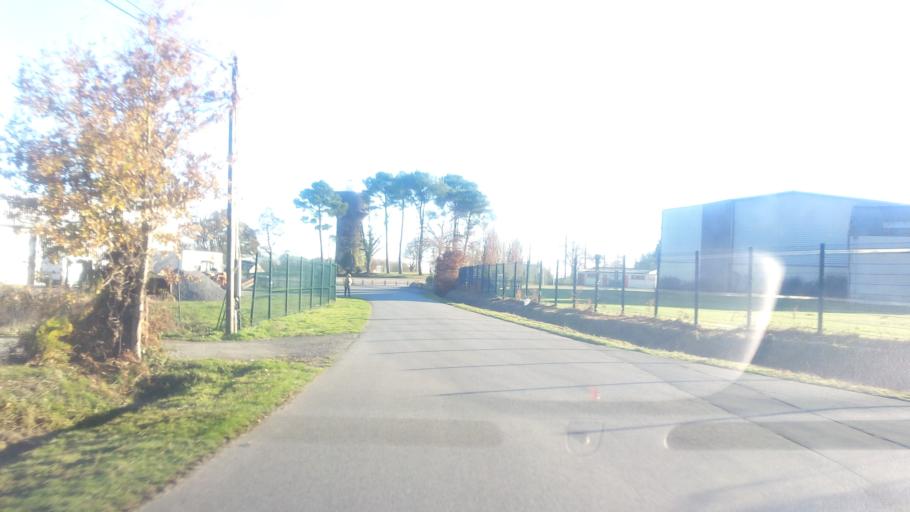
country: FR
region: Brittany
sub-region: Departement du Morbihan
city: Peillac
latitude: 47.7185
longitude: -2.2280
